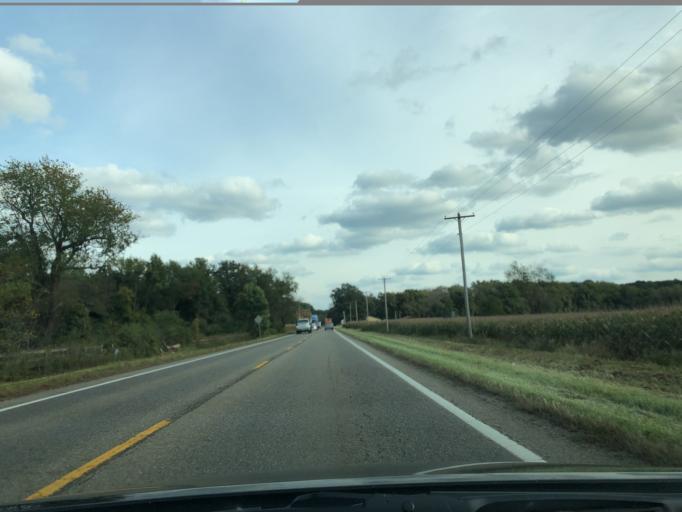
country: US
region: Ohio
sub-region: Stark County
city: Beach City
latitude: 40.6389
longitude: -81.5733
